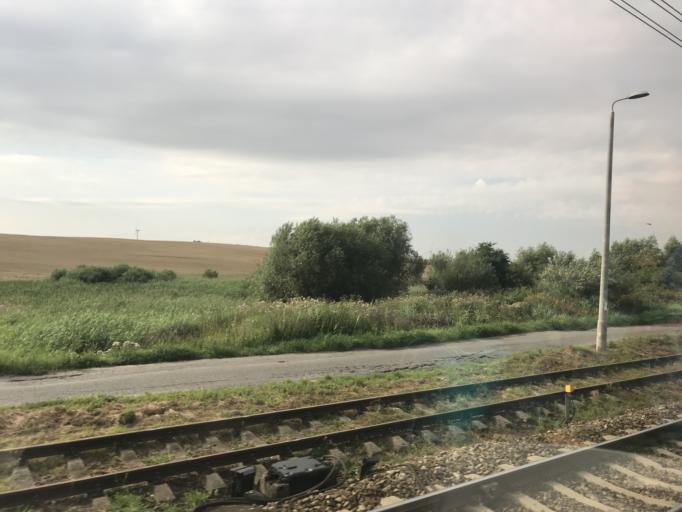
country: PL
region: Pomeranian Voivodeship
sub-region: Powiat tczewski
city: Pelplin
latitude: 53.9331
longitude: 18.7195
